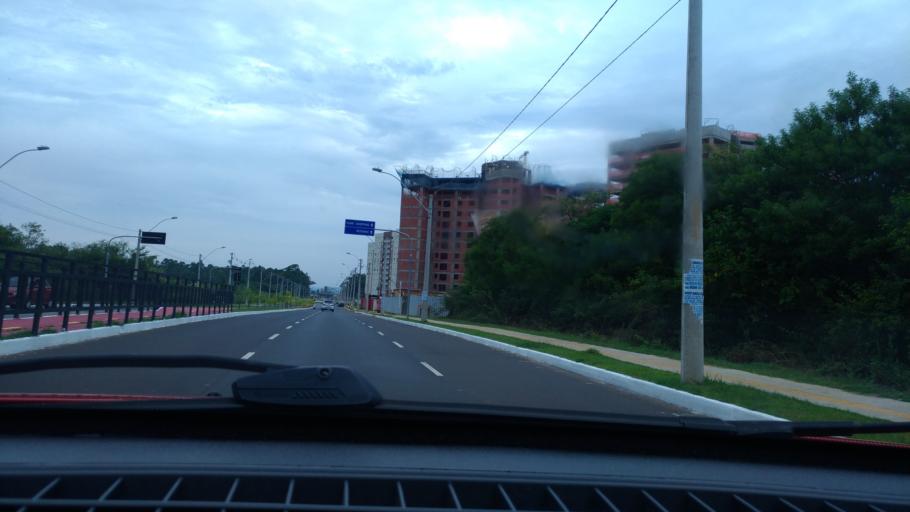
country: BR
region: Rio Grande do Sul
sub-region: Canoas
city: Canoas
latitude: -29.9060
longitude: -51.1649
